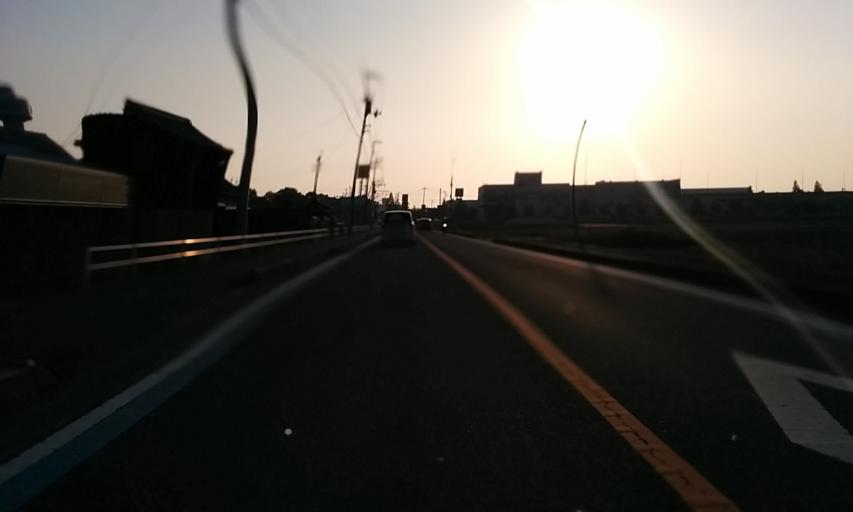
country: JP
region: Ehime
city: Masaki-cho
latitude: 33.7717
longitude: 132.7212
